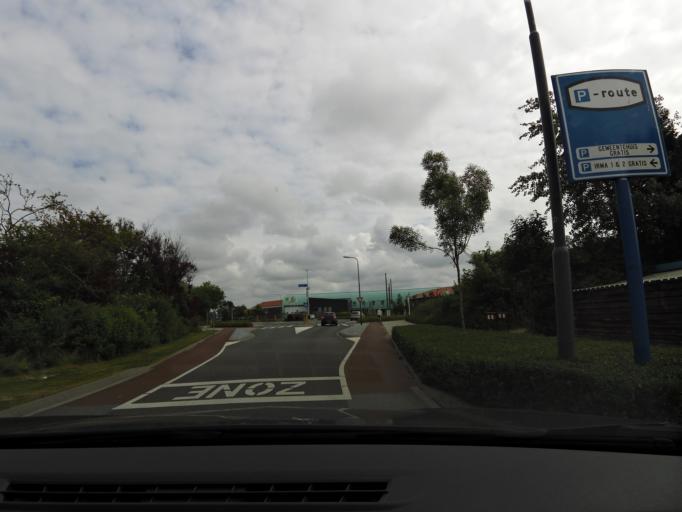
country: NL
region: Zeeland
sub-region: Gemeente Middelburg
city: Middelburg
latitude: 51.5605
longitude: 3.5009
